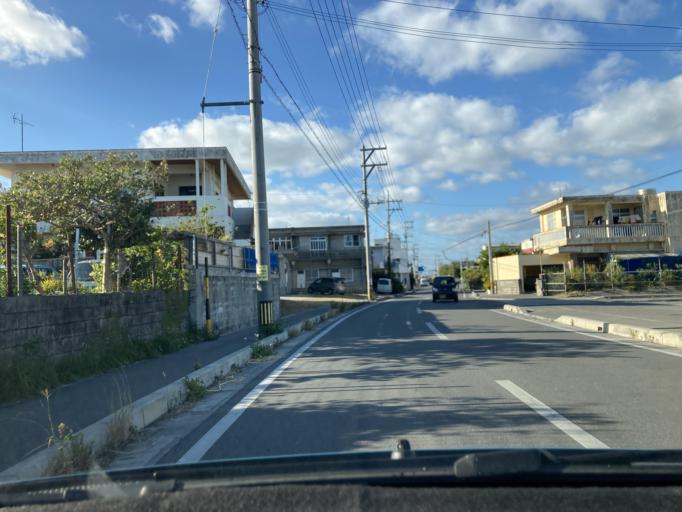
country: JP
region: Okinawa
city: Katsuren-haebaru
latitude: 26.3260
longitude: 127.9033
